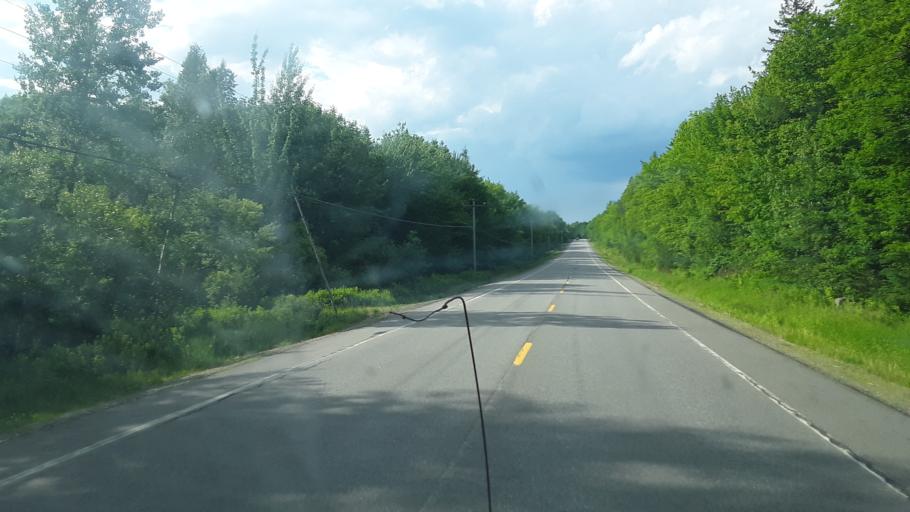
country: US
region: Maine
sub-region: Washington County
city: Machias
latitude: 45.0059
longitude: -67.5533
